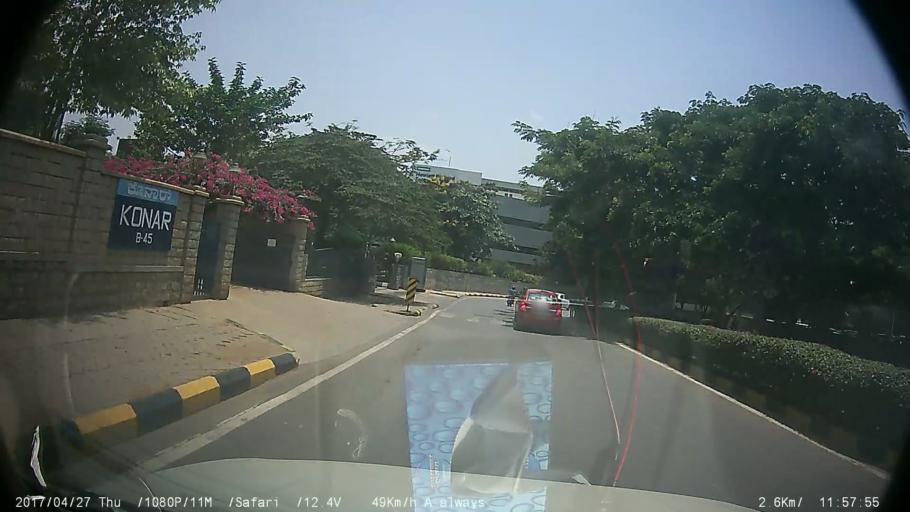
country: IN
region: Karnataka
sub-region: Bangalore Urban
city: Bangalore
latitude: 12.8533
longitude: 77.6604
